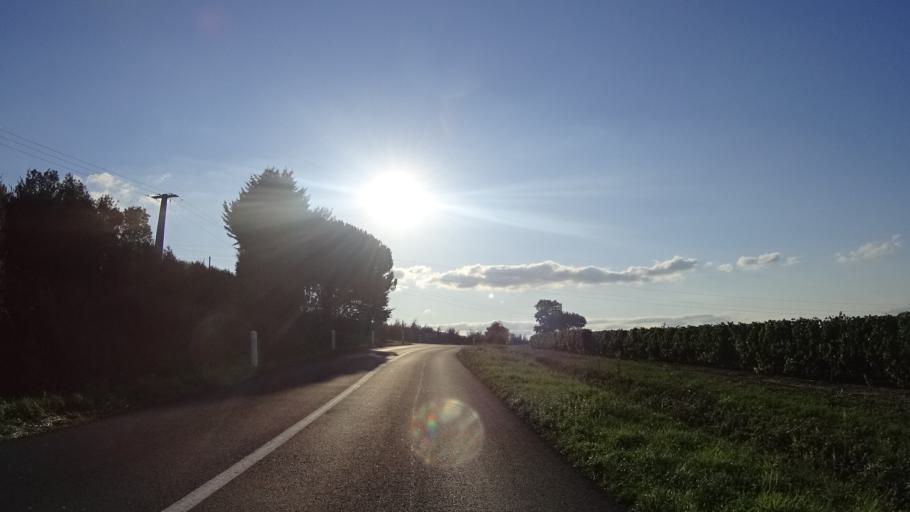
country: FR
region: Pays de la Loire
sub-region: Departement de Maine-et-Loire
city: Bouzille
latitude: 47.3416
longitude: -1.1332
